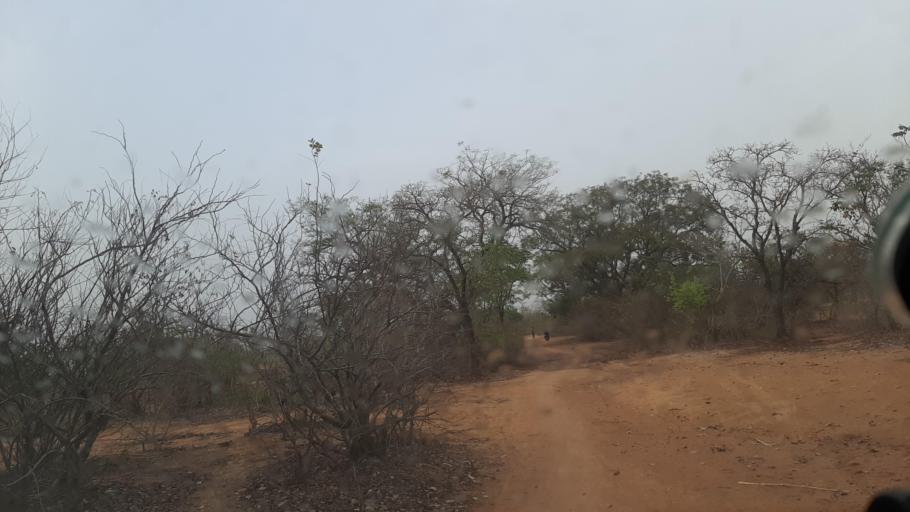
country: BF
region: Boucle du Mouhoun
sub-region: Province des Banwa
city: Salanso
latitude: 11.8632
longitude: -4.4393
